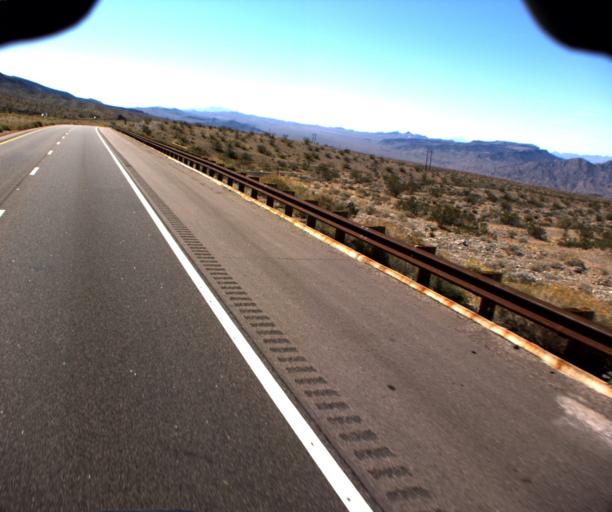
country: US
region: Nevada
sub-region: Clark County
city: Boulder City
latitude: 35.9343
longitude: -114.6375
